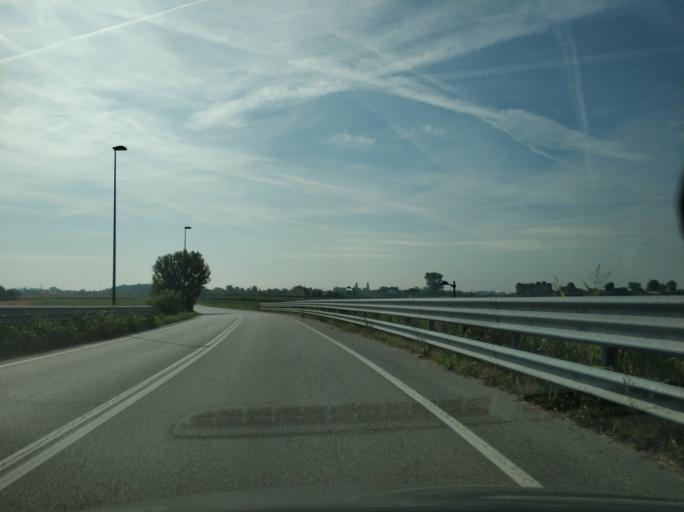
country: IT
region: Veneto
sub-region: Provincia di Padova
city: Este
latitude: 45.2119
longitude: 11.6874
